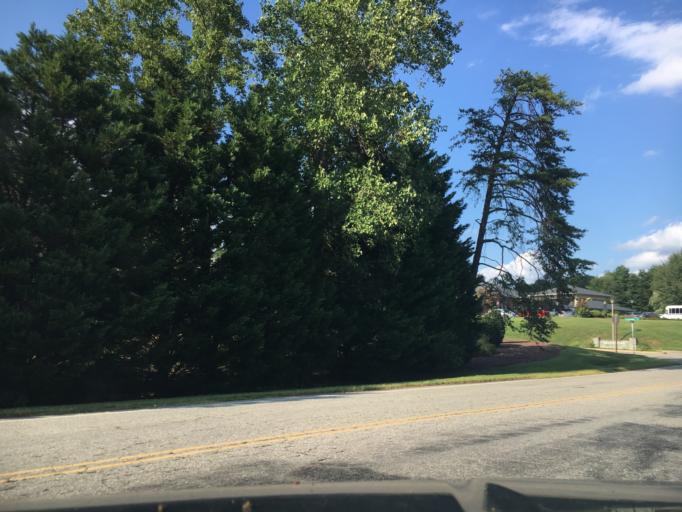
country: US
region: Virginia
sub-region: Halifax County
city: South Boston
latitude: 36.7135
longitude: -78.9177
